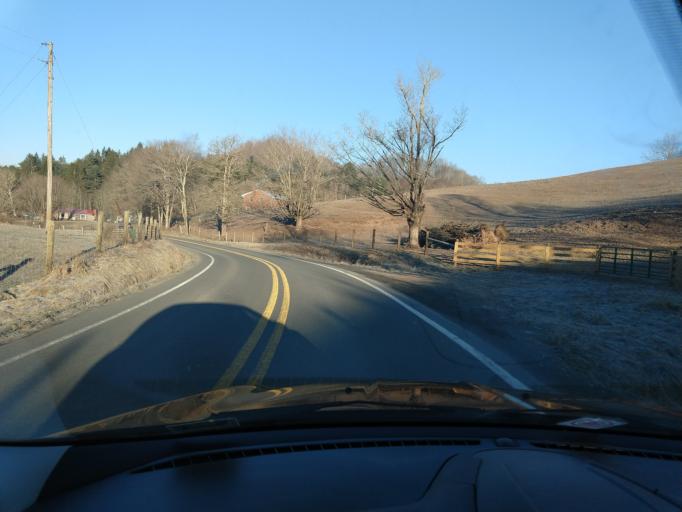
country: US
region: West Virginia
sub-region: Greenbrier County
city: Rainelle
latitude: 37.8692
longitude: -80.7253
